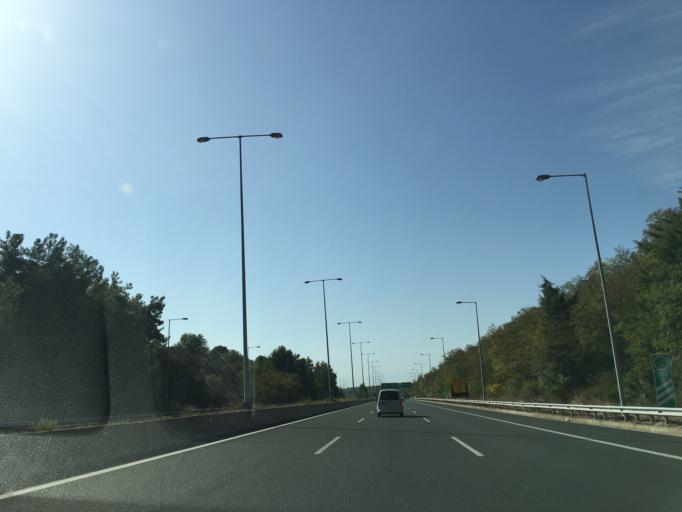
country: GR
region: Central Macedonia
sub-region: Nomos Pierias
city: Makrygialos
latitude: 40.4254
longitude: 22.5894
